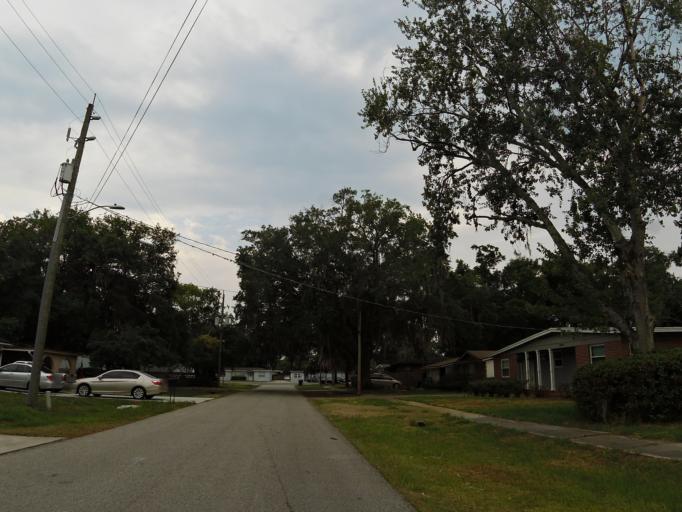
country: US
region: Florida
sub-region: Duval County
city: Jacksonville
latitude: 30.2620
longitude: -81.6361
